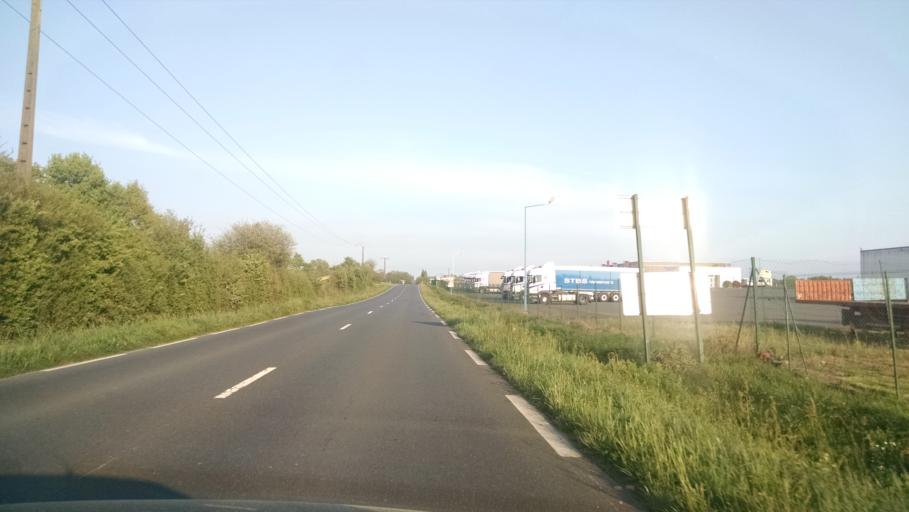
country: FR
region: Pays de la Loire
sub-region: Departement de la Loire-Atlantique
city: Getigne
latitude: 47.0754
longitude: -1.2319
